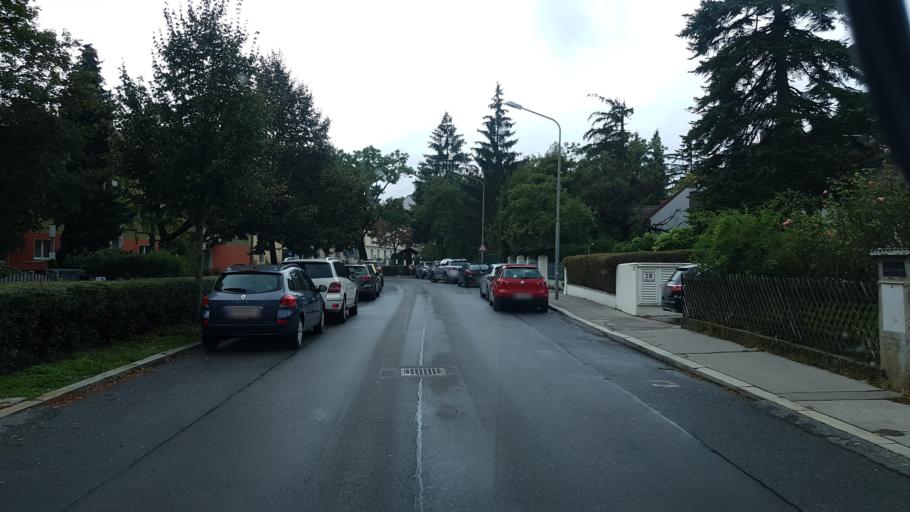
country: AT
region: Lower Austria
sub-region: Politischer Bezirk Wien-Umgebung
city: Klosterneuburg
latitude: 48.2496
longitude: 16.3263
